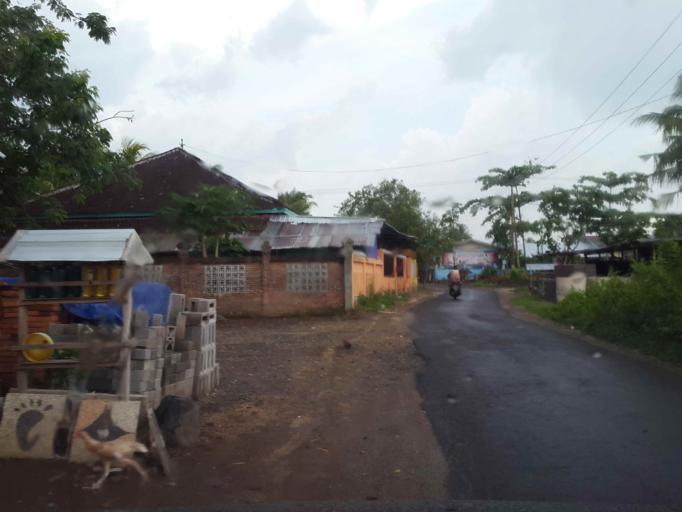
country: ID
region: West Nusa Tenggara
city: Kekeri
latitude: -8.5581
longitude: 116.1246
